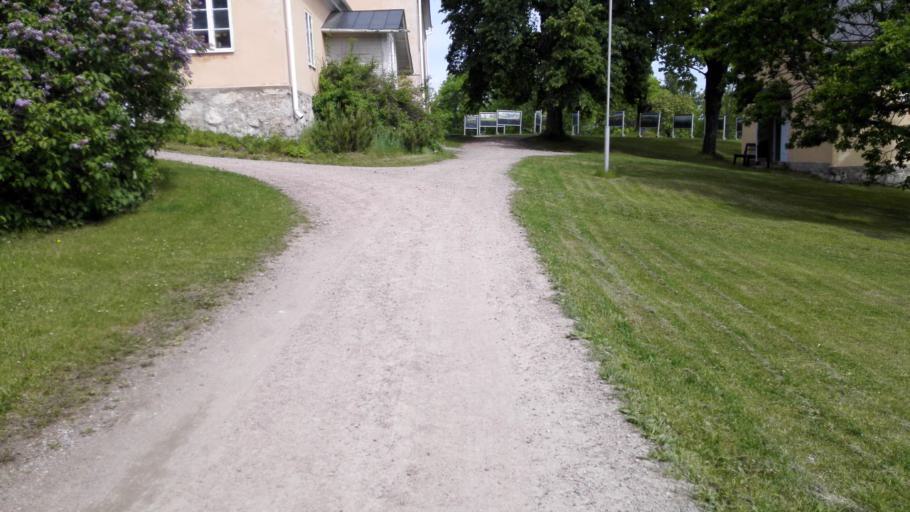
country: FI
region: Varsinais-Suomi
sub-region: Aboland-Turunmaa
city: Nagu
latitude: 60.2393
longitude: 21.9627
